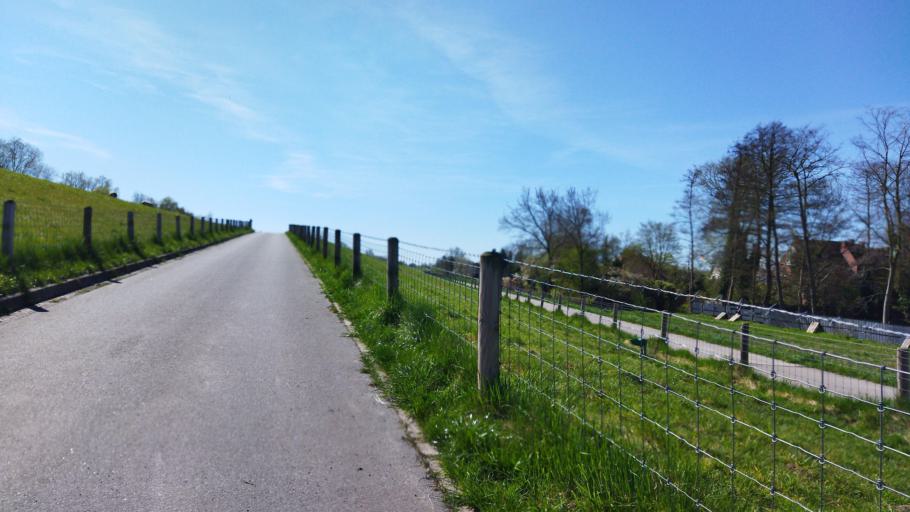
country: DE
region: Lower Saxony
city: Brake (Unterweser)
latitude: 53.3025
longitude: 8.4864
